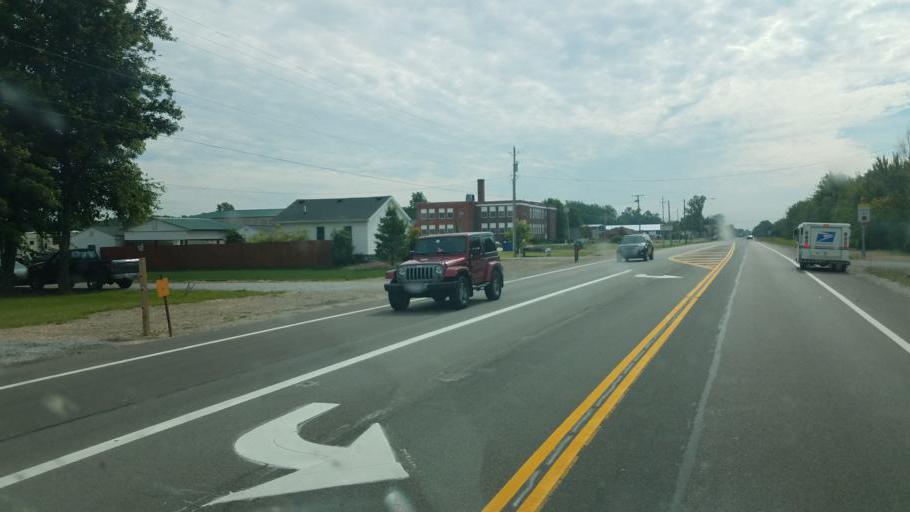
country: US
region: Ohio
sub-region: Lorain County
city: Eaton Estates
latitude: 41.3142
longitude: -82.0166
